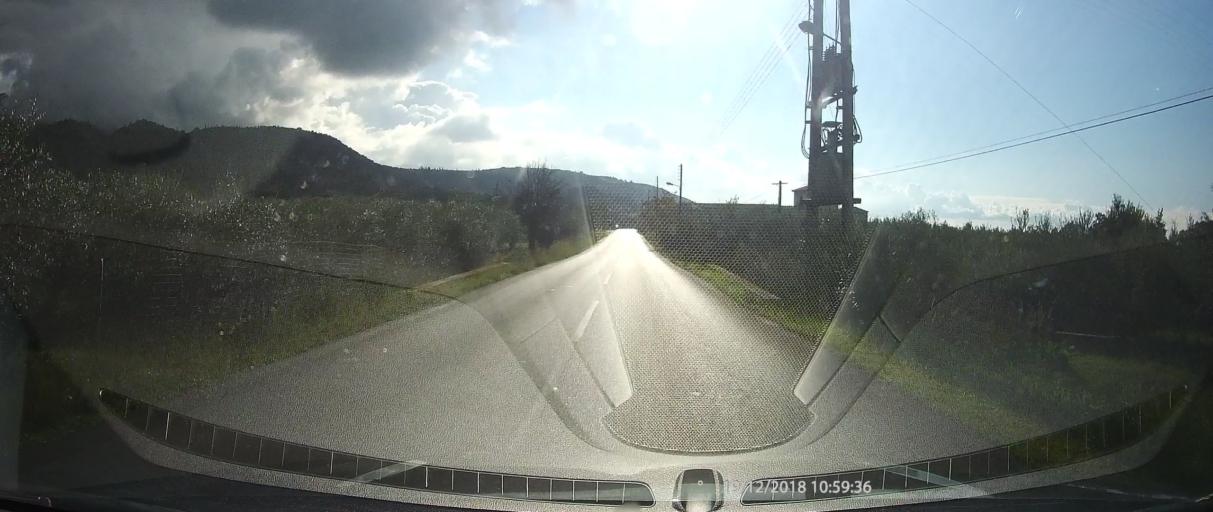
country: GR
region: Peloponnese
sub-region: Nomos Messinias
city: Kardamyli
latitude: 36.8943
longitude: 22.2301
